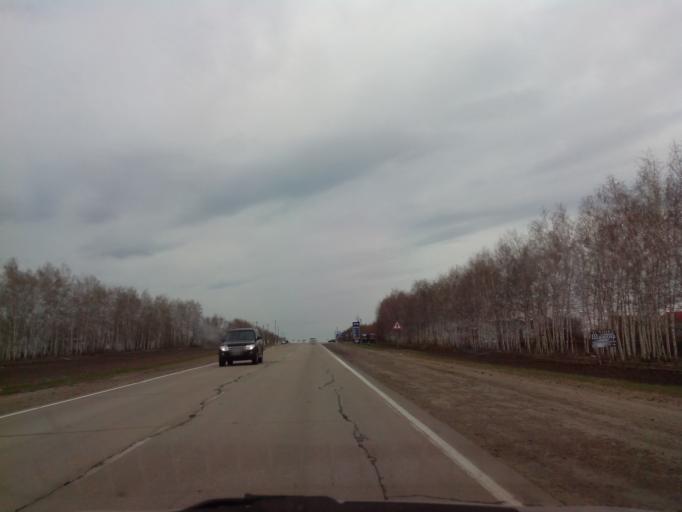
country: RU
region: Tambov
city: Znamenka
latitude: 52.4003
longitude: 41.3927
